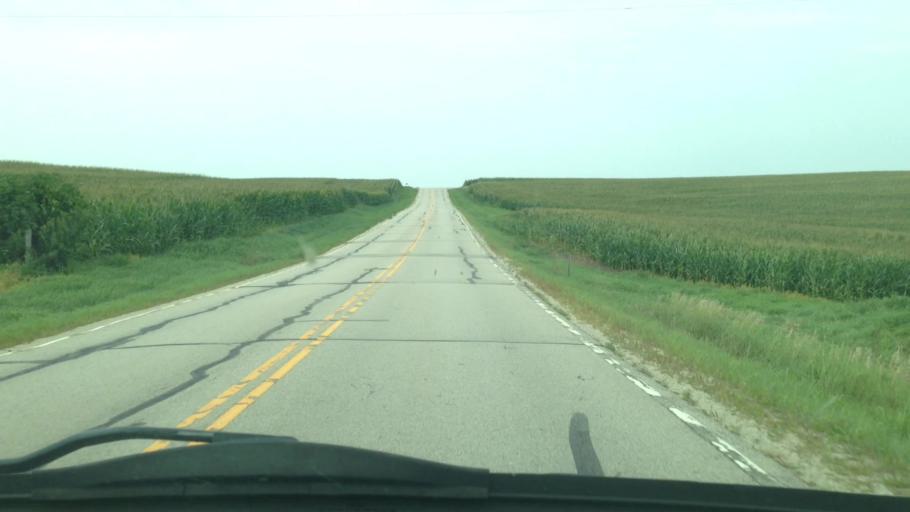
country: US
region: Minnesota
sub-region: Fillmore County
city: Preston
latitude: 43.7888
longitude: -91.9498
